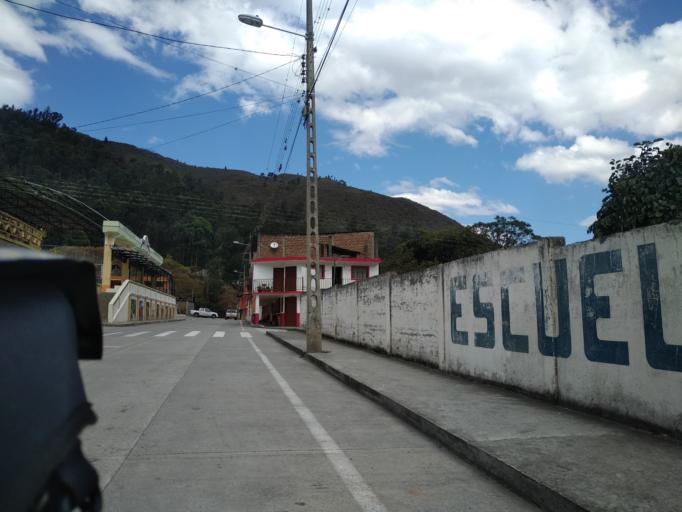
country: EC
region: Zamora-Chinchipe
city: Zamora
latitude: -4.3643
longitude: -79.1764
